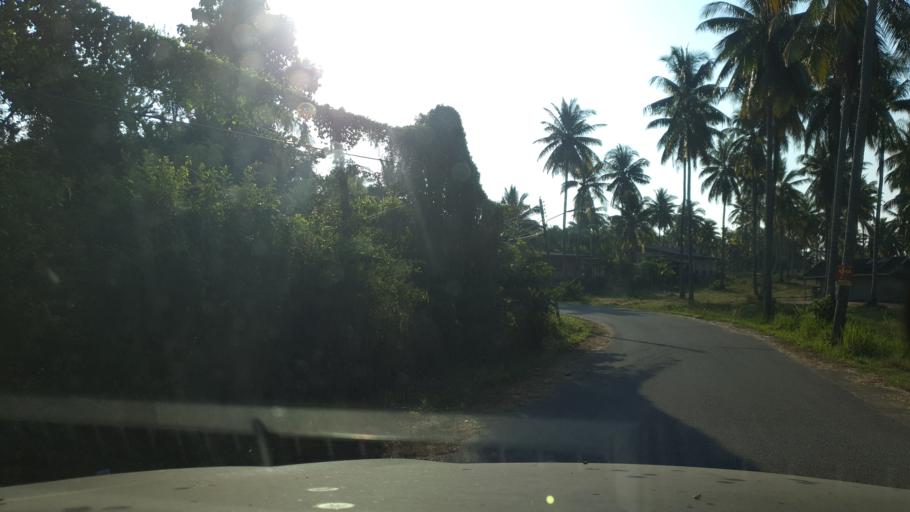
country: TH
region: Prachuap Khiri Khan
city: Bang Saphan
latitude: 11.2131
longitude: 99.5760
